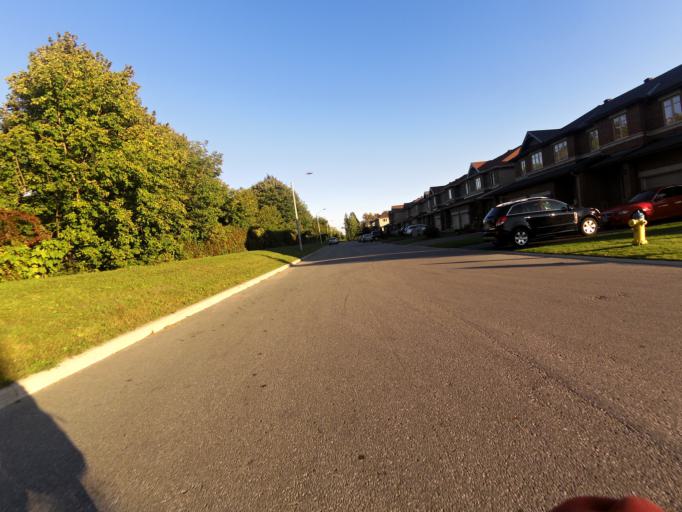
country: CA
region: Ontario
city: Bells Corners
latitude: 45.3631
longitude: -75.9276
